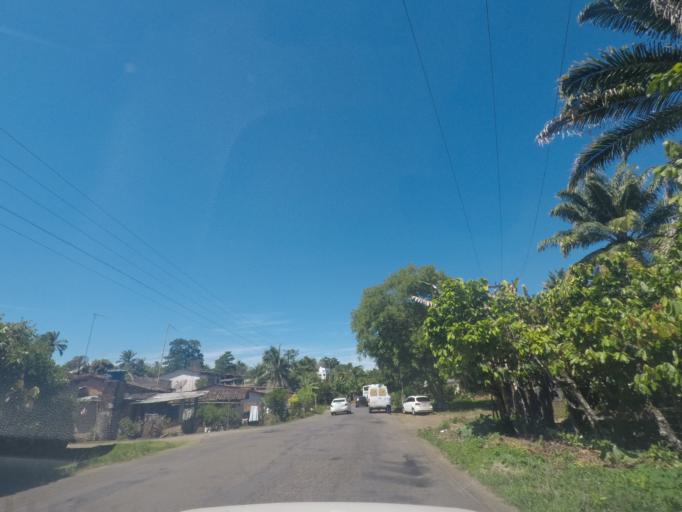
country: BR
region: Bahia
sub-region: Valenca
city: Valenca
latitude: -13.4200
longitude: -39.0782
